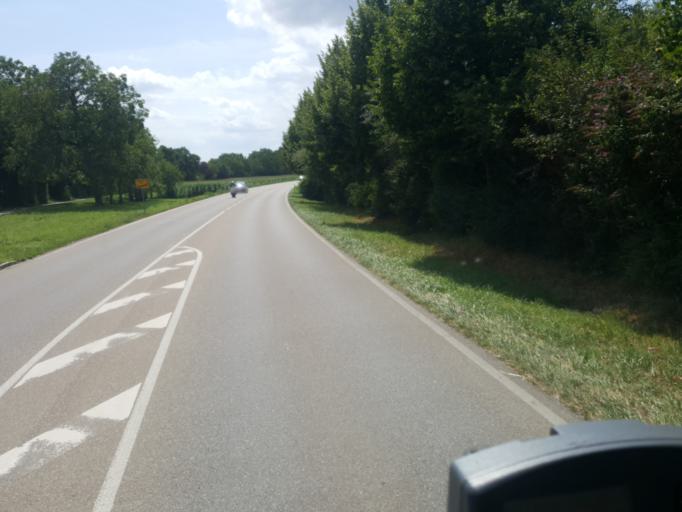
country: DE
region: Baden-Wuerttemberg
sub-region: Freiburg Region
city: Buggingen
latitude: 47.8577
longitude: 7.6383
